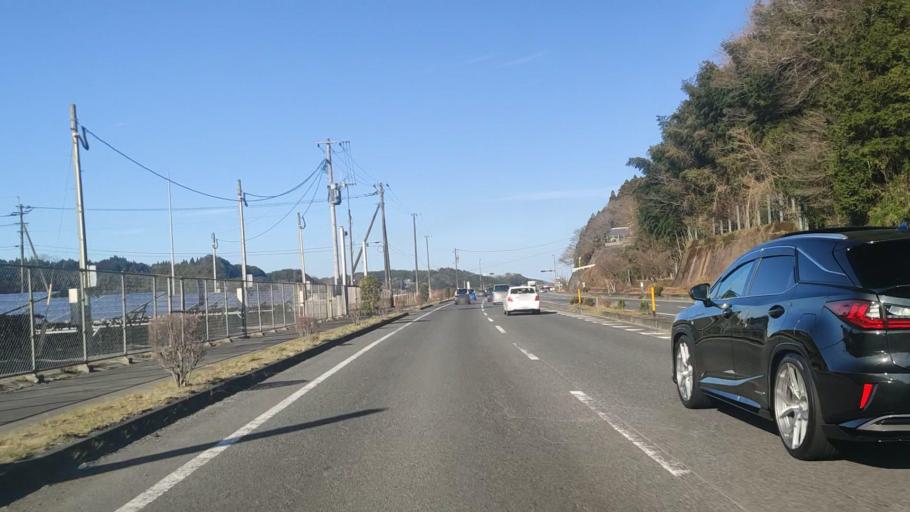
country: JP
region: Oita
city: Oita
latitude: 33.1178
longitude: 131.6536
